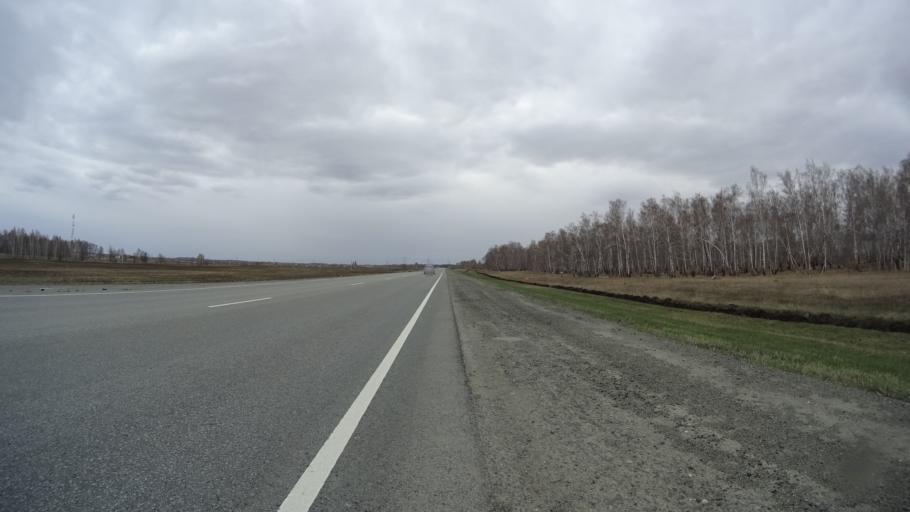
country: RU
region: Chelyabinsk
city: Krasnogorskiy
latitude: 54.6889
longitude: 61.2483
